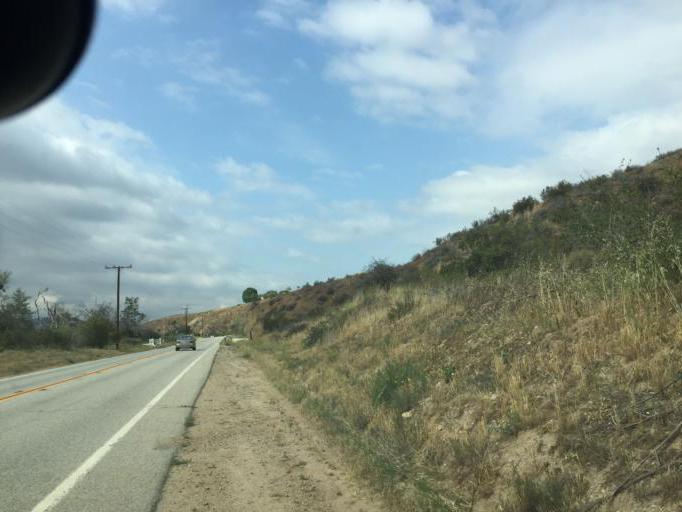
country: US
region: California
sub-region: Los Angeles County
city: Green Valley
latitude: 34.4989
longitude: -118.4561
